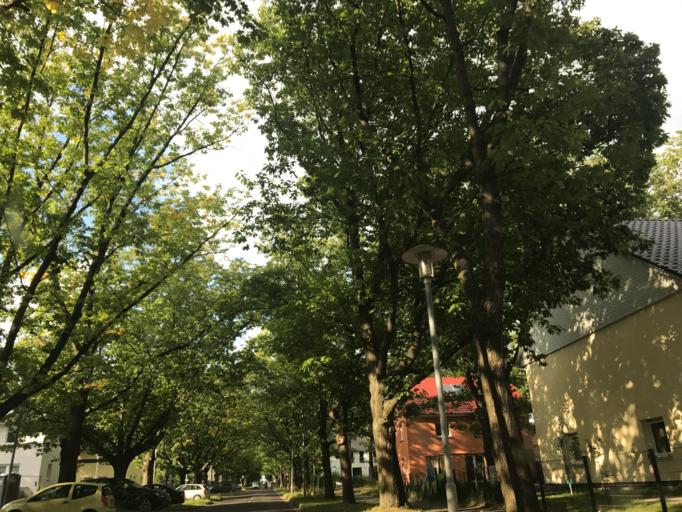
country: DE
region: Brandenburg
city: Dallgow-Doeberitz
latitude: 52.5362
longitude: 13.0549
